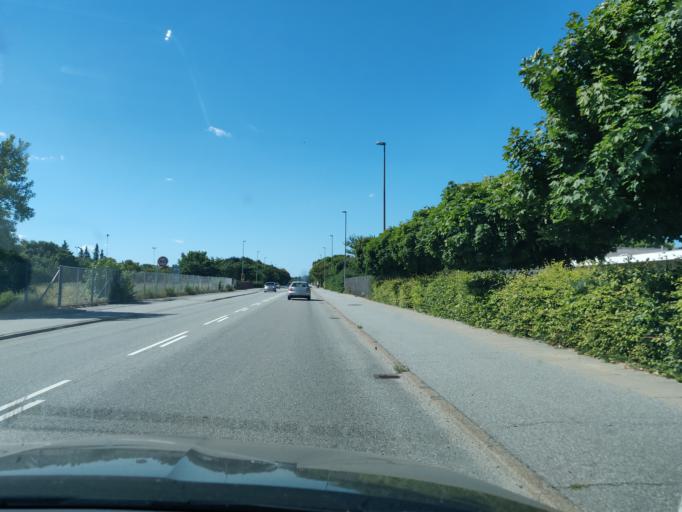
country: DK
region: North Denmark
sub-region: Alborg Kommune
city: Aalborg
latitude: 57.0741
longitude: 9.9506
